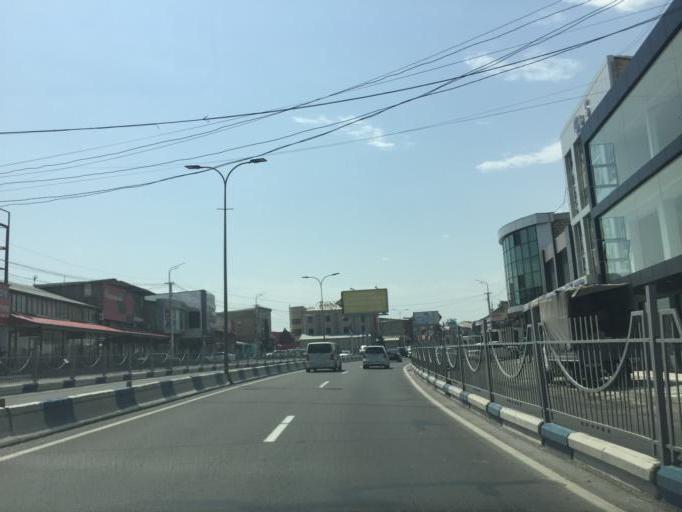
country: AM
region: Ararat
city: Argavand
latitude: 40.1581
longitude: 44.4351
